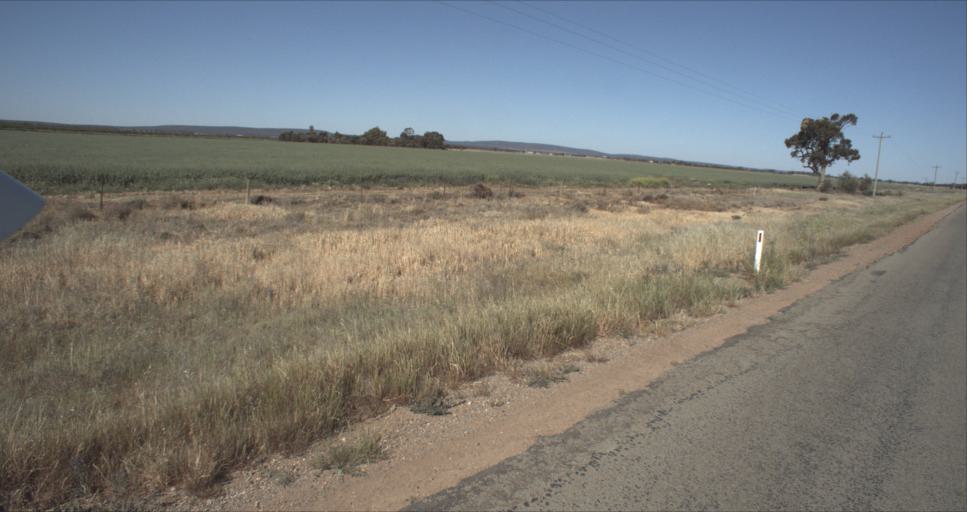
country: AU
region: New South Wales
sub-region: Leeton
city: Leeton
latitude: -34.4826
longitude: 146.3732
